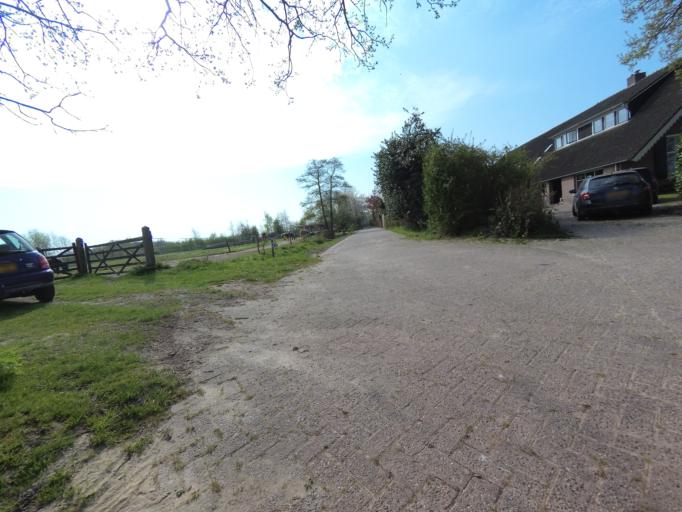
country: NL
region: Gelderland
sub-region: Gemeente Barneveld
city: Zwartebroek
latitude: 52.1604
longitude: 5.4734
